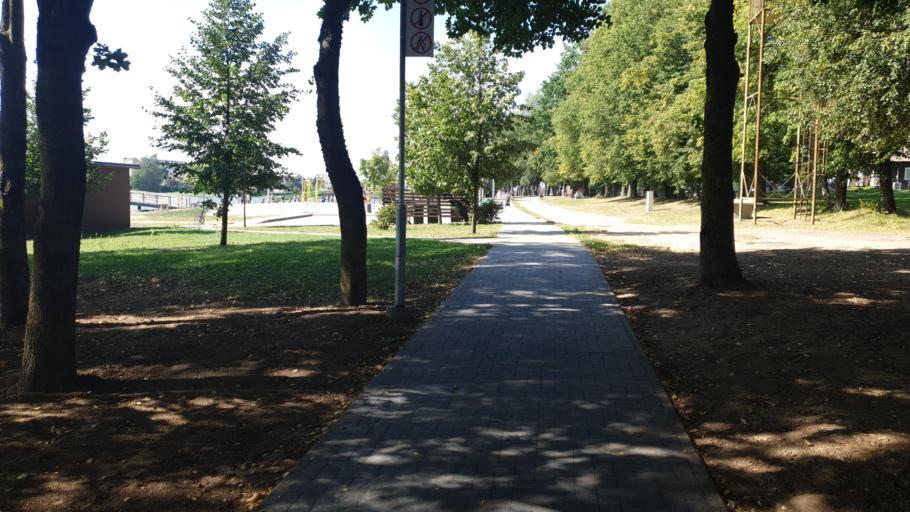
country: LT
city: Sirvintos
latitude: 55.0429
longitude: 24.9619
